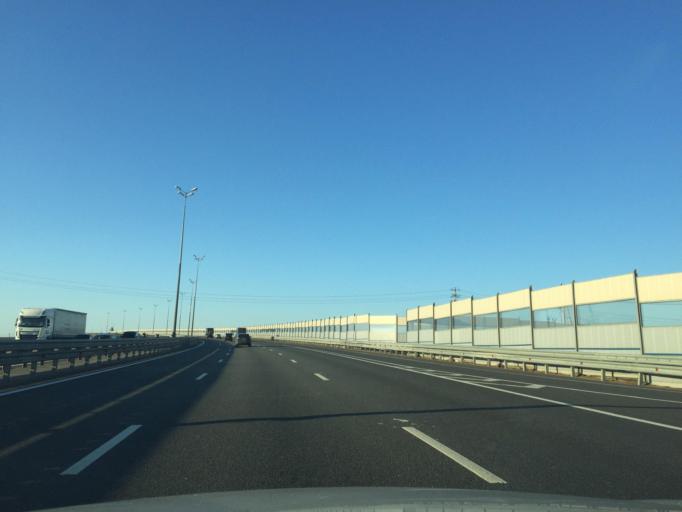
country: RU
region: Leningrad
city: Maloye Verevo
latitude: 59.6466
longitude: 30.2271
